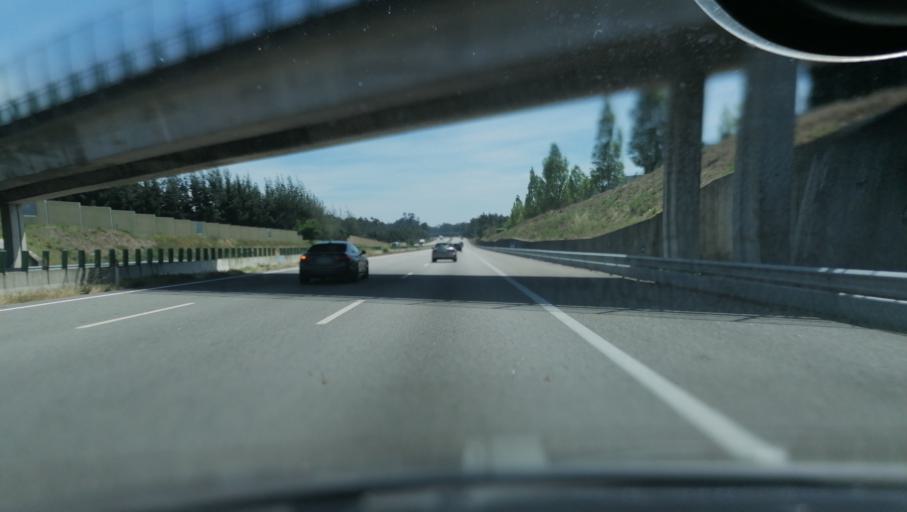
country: PT
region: Aveiro
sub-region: Ovar
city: Valega
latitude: 40.8789
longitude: -8.5608
